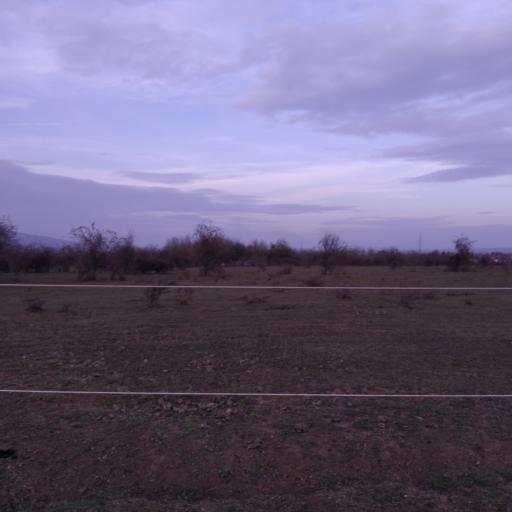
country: HU
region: Pest
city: Pomaz
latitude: 47.6228
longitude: 19.0247
